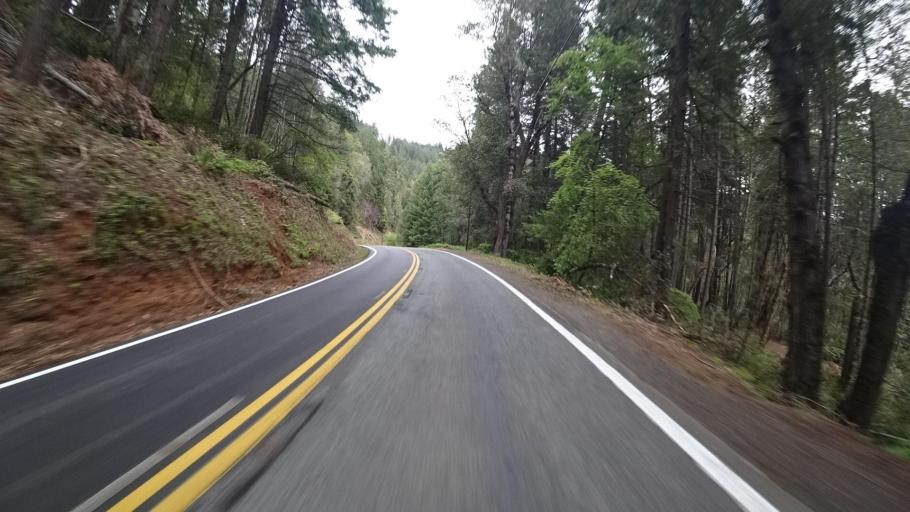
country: US
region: California
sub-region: Humboldt County
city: Willow Creek
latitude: 41.0061
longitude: -123.6485
